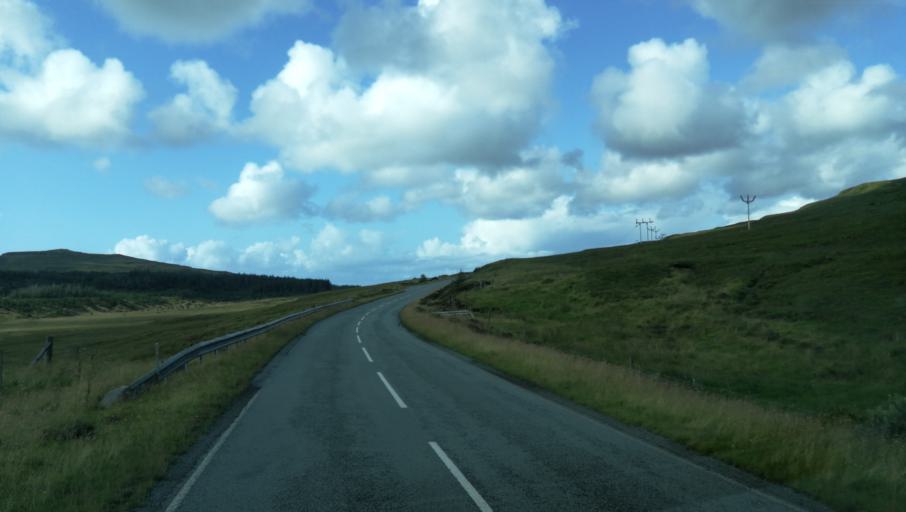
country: GB
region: Scotland
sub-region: Highland
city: Isle of Skye
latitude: 57.4491
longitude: -6.5436
